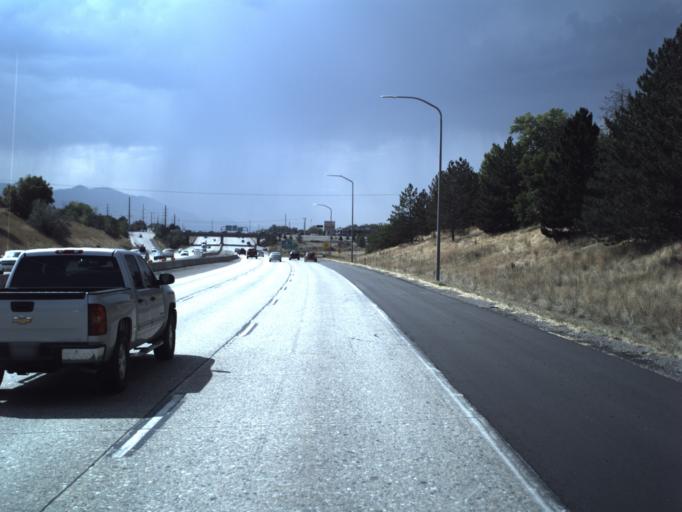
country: US
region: Utah
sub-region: Salt Lake County
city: Willard
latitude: 40.7197
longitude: -111.8469
